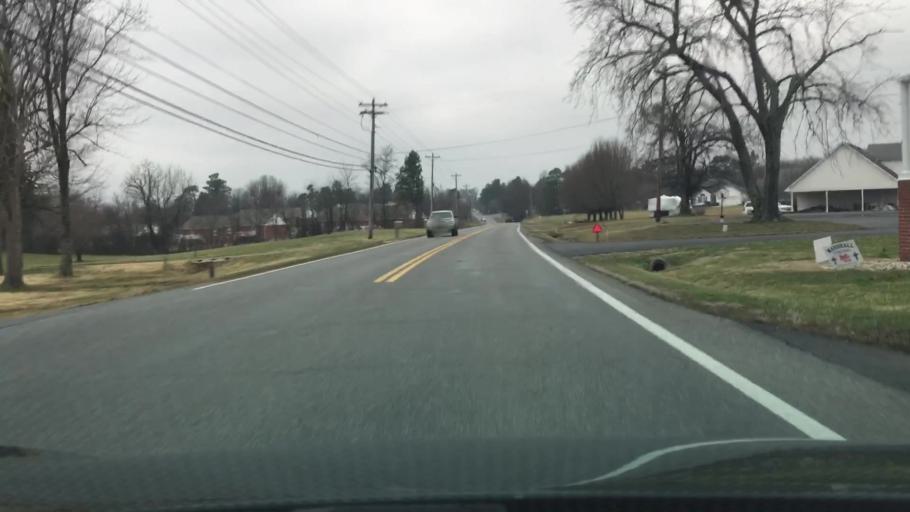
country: US
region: Kentucky
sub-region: Marshall County
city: Benton
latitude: 36.9429
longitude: -88.3626
